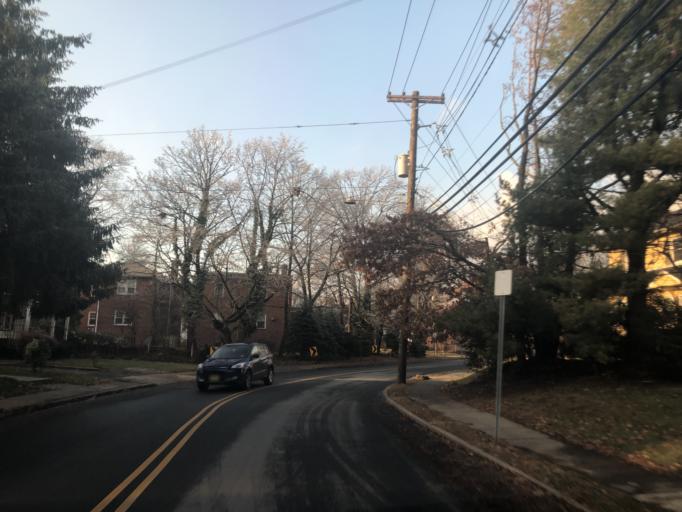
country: US
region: New Jersey
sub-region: Union County
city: Union
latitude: 40.7169
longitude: -74.2547
